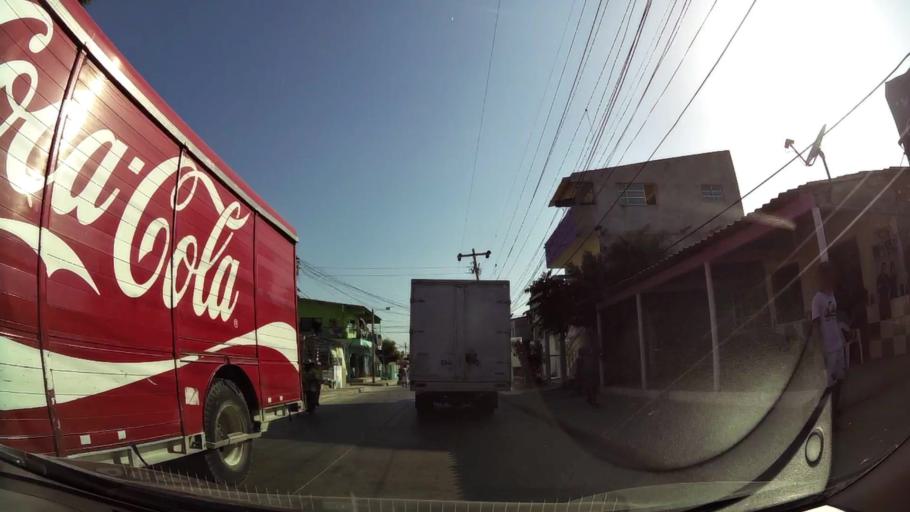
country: CO
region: Bolivar
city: Cartagena
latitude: 10.4119
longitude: -75.5000
